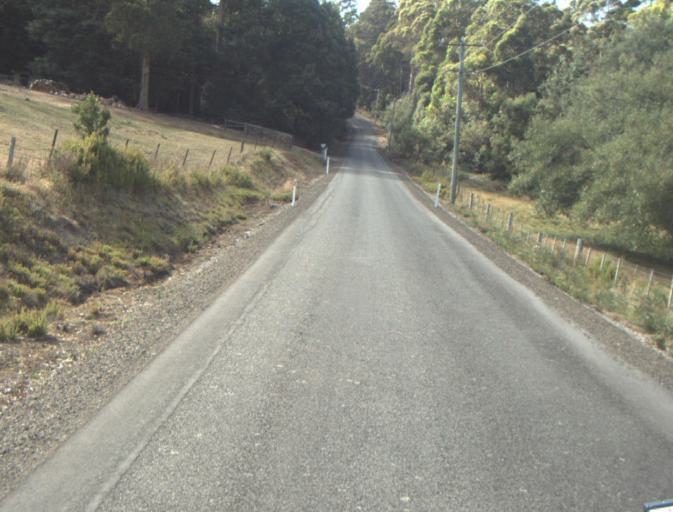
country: AU
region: Tasmania
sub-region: Launceston
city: Mayfield
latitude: -41.2839
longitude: 147.1978
